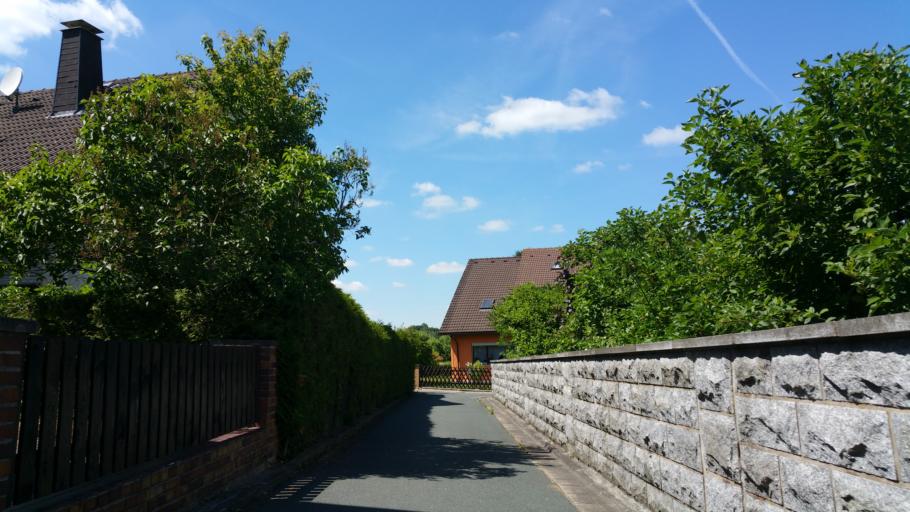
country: DE
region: Bavaria
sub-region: Upper Franconia
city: Schwarzenbach an der Saale
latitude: 50.2202
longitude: 11.9273
